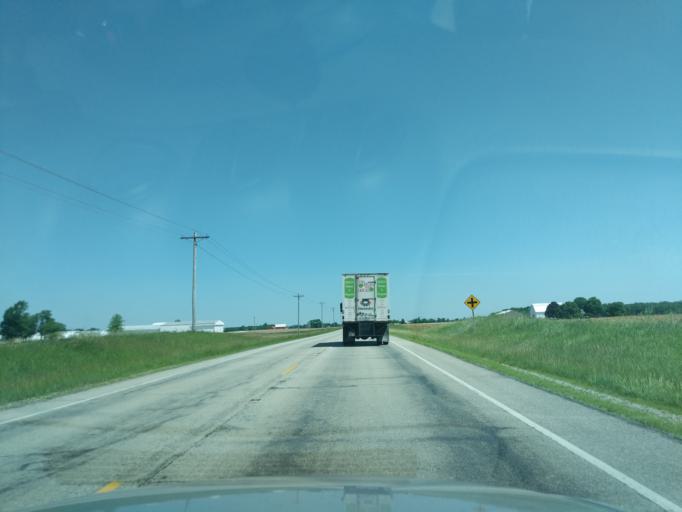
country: US
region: Indiana
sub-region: Huntington County
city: Roanoke
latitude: 41.0313
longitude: -85.4707
